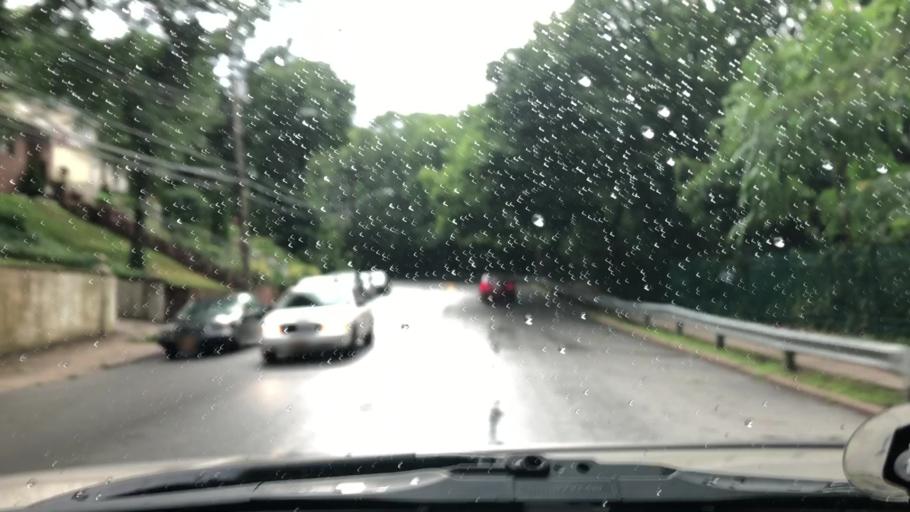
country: US
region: New Jersey
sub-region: Hudson County
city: Bayonne
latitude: 40.6354
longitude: -74.0949
